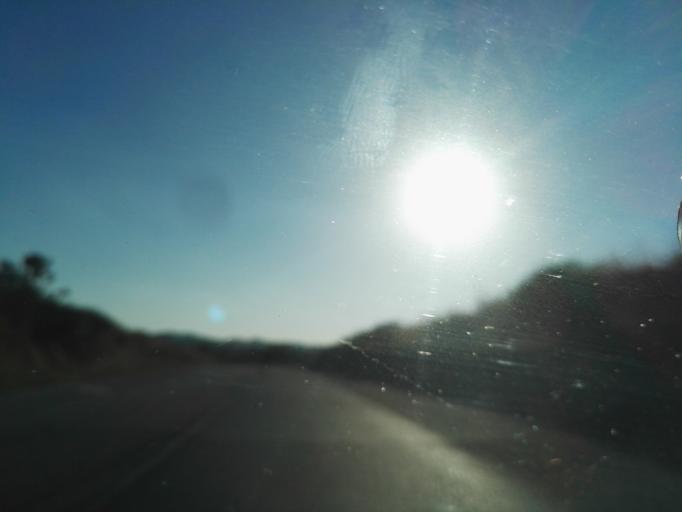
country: PT
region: Evora
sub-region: Vila Vicosa
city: Vila Vicosa
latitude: 38.8371
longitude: -7.4012
